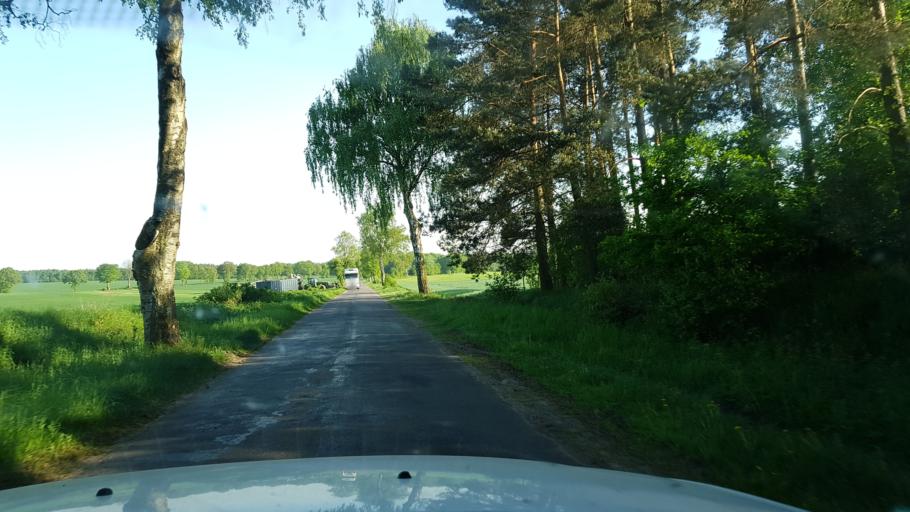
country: PL
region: West Pomeranian Voivodeship
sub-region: Powiat lobeski
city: Dobra
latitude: 53.6042
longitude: 15.3310
